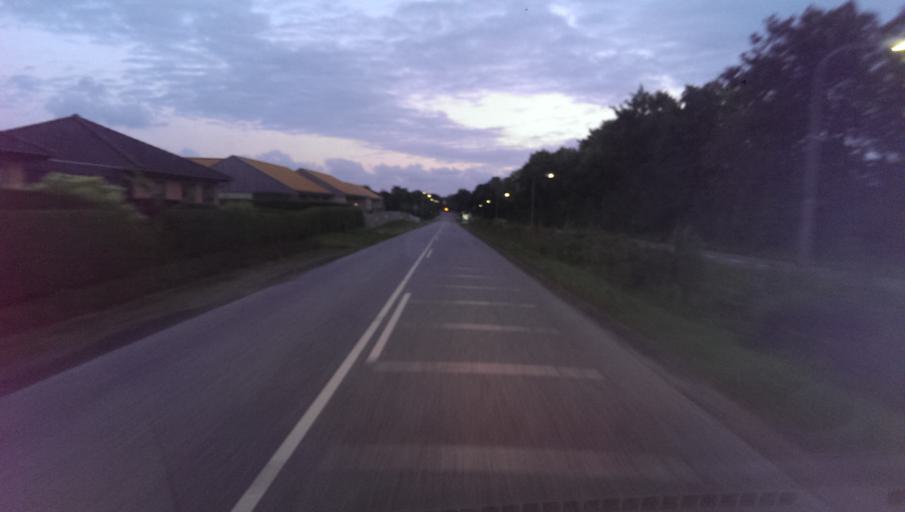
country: DK
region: South Denmark
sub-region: Esbjerg Kommune
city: Esbjerg
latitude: 55.5305
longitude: 8.4679
